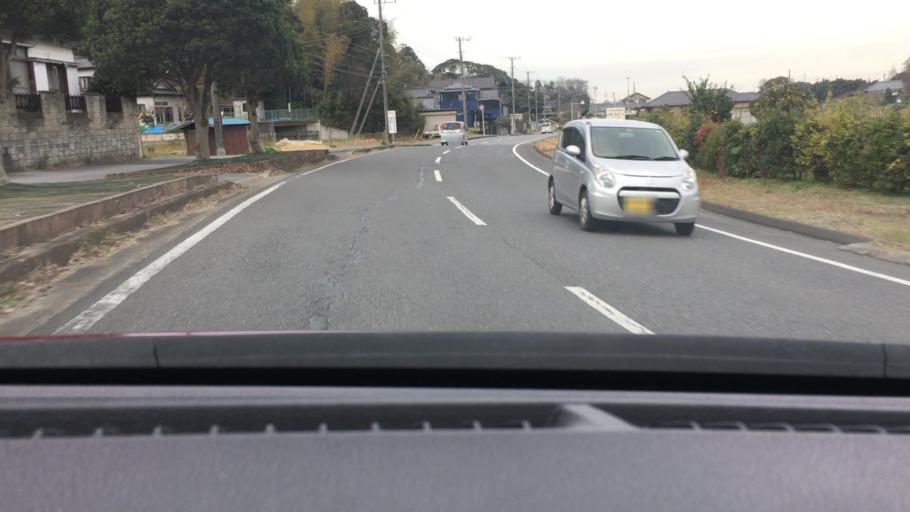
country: JP
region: Chiba
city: Ichihara
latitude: 35.4708
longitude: 140.0639
